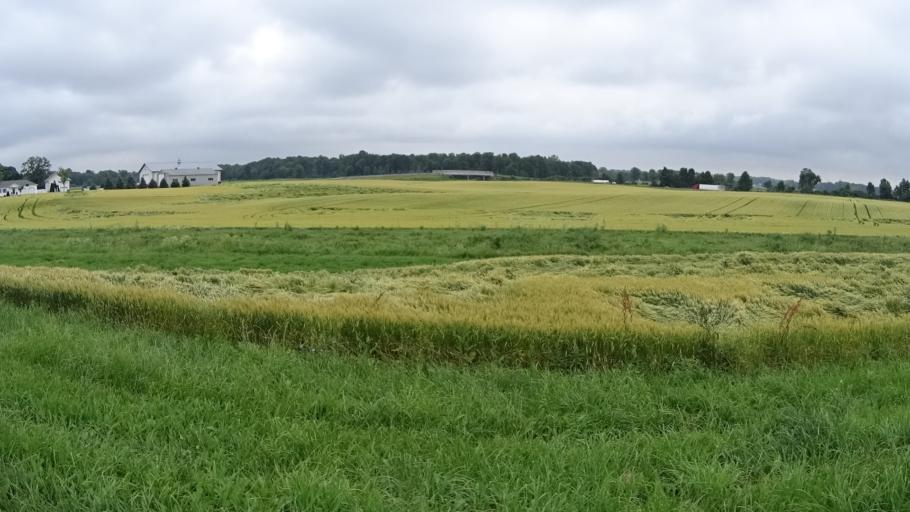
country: US
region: Ohio
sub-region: Erie County
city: Huron
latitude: 41.3287
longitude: -82.5389
